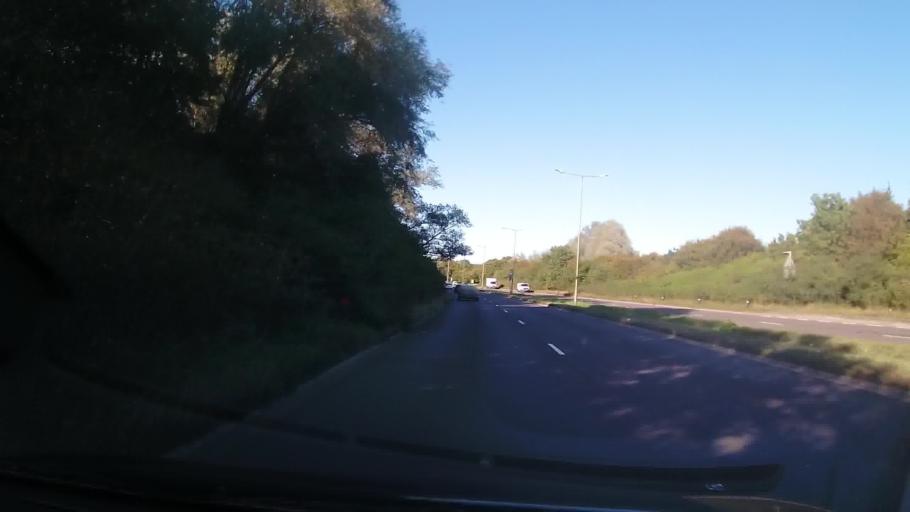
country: GB
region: England
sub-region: Buckinghamshire
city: Beaconsfield
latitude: 51.5977
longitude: -0.6250
